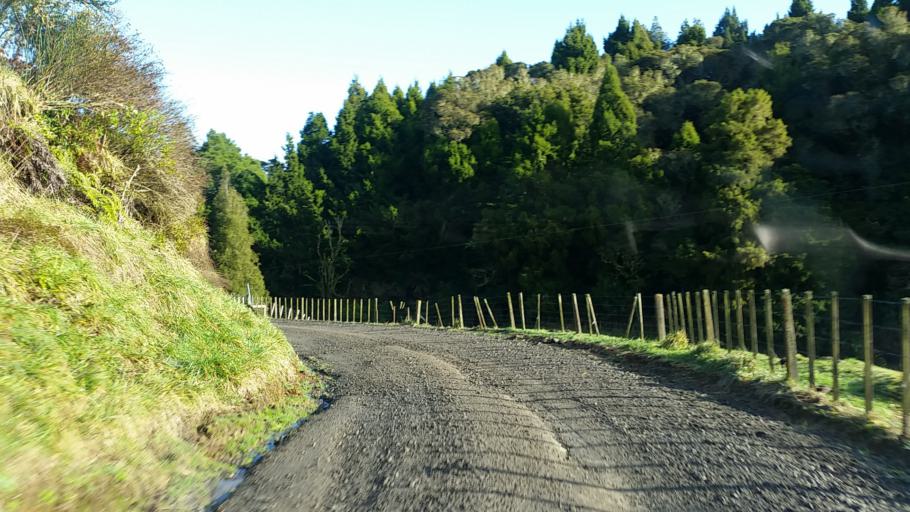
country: NZ
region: Taranaki
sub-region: South Taranaki District
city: Eltham
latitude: -39.2476
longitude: 174.3786
